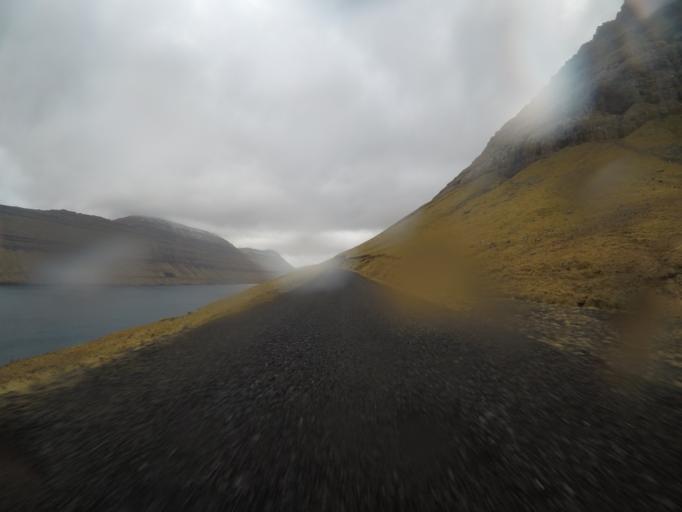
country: FO
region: Nordoyar
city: Klaksvik
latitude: 62.3317
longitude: -6.5737
